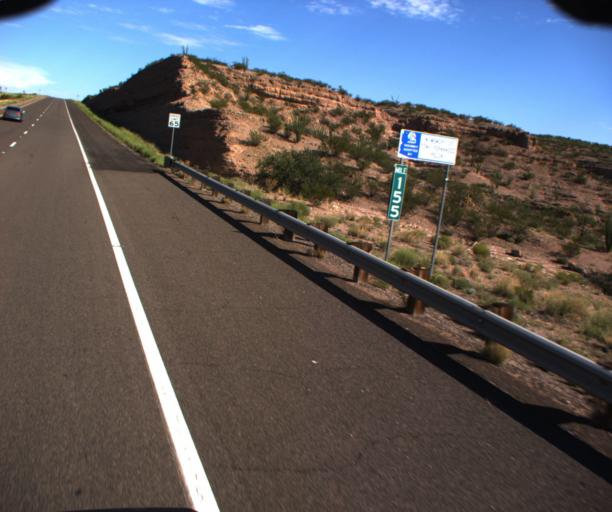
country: US
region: Arizona
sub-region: Greenlee County
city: Clifton
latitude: 32.9550
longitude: -109.2298
